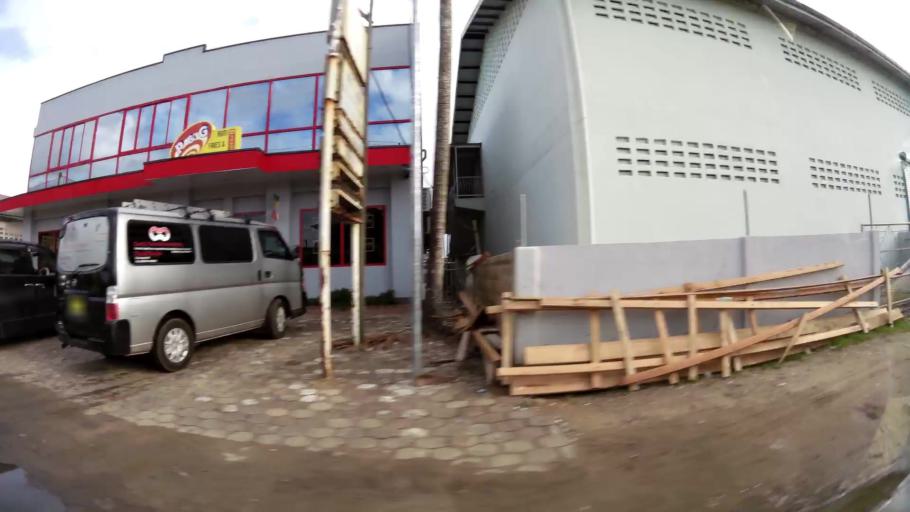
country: SR
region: Paramaribo
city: Paramaribo
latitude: 5.8471
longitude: -55.2379
